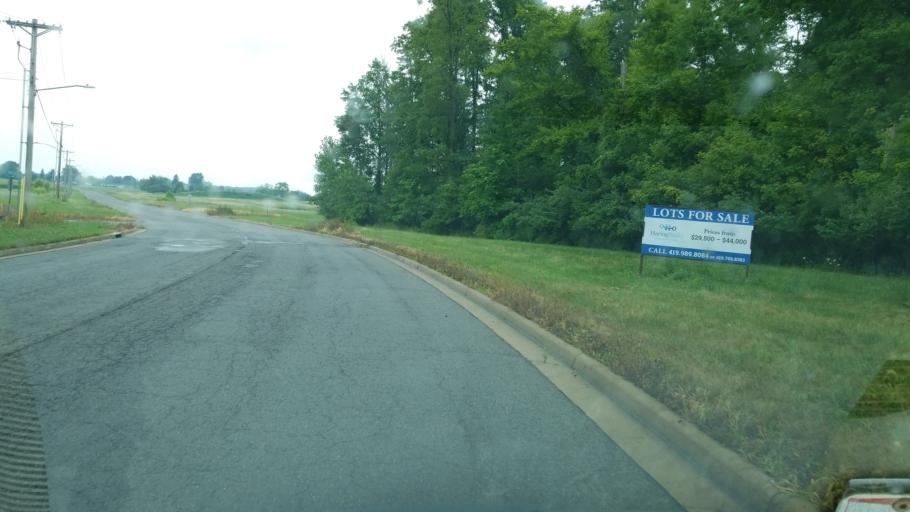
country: US
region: Ohio
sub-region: Richland County
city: Shelby
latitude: 40.8723
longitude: -82.6361
